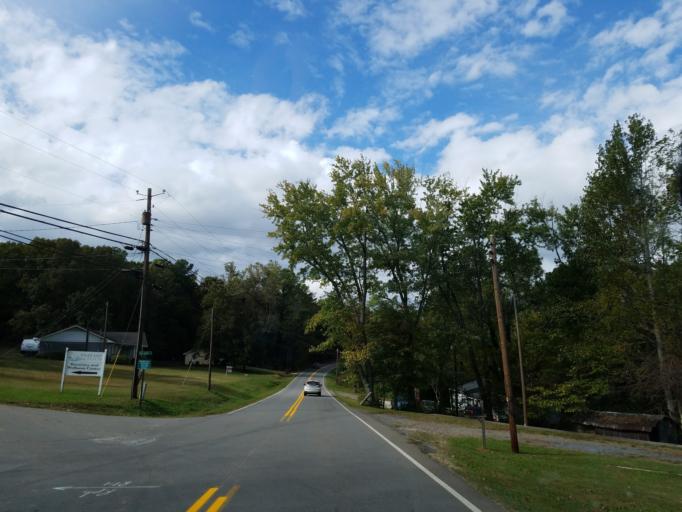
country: US
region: Georgia
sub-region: Pickens County
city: Jasper
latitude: 34.4267
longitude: -84.4198
